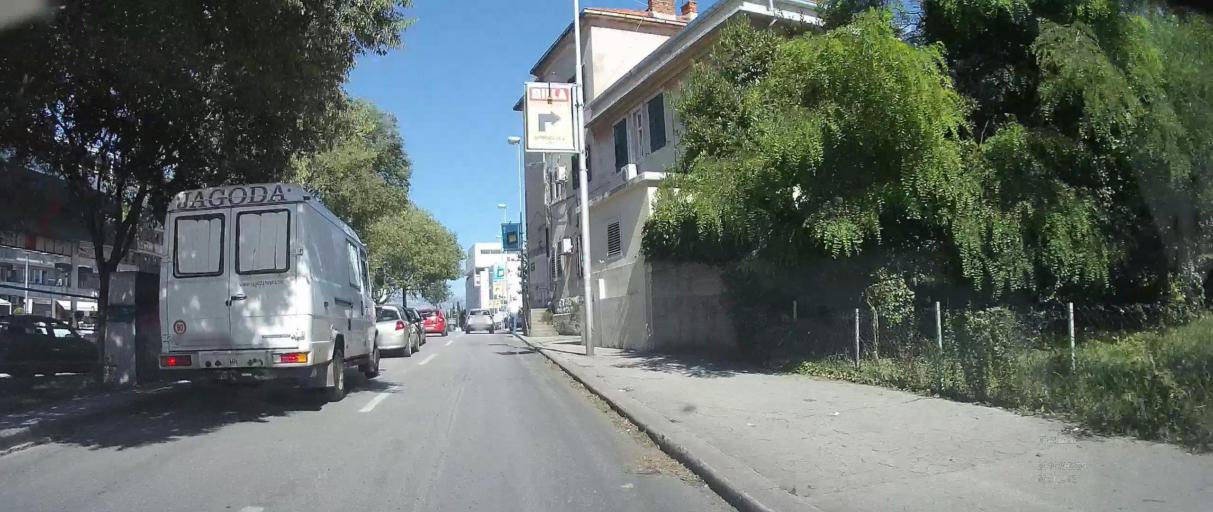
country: HR
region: Splitsko-Dalmatinska
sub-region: Grad Split
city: Split
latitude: 43.5049
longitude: 16.4529
